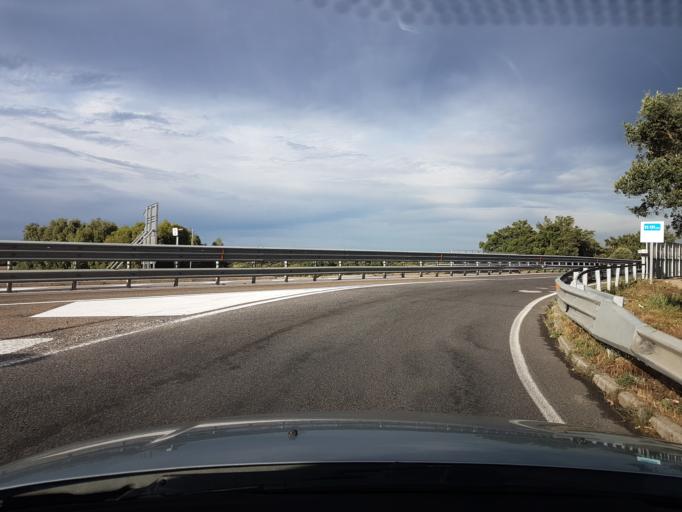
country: IT
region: Sardinia
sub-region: Provincia di Oristano
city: Abbasanta
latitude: 40.1140
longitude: 8.7969
